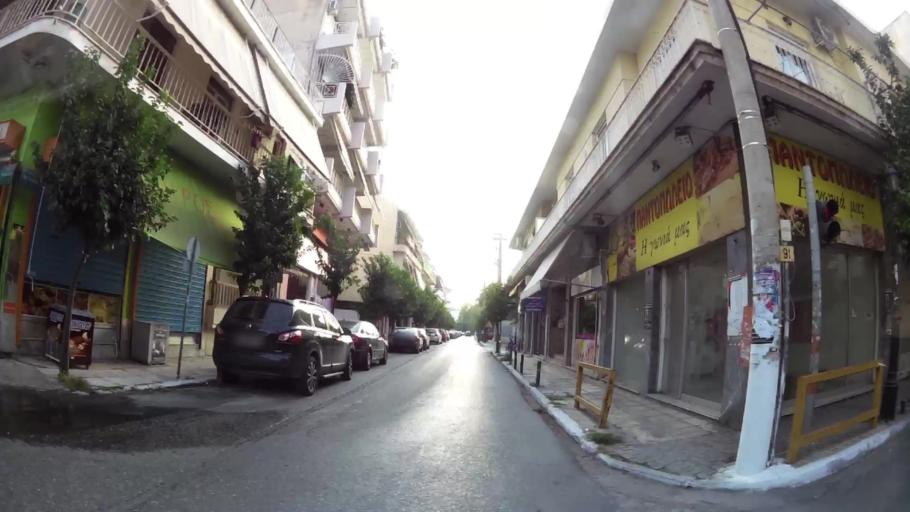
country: GR
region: Attica
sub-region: Nomarchia Athinas
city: Tavros
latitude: 37.9657
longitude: 23.7021
